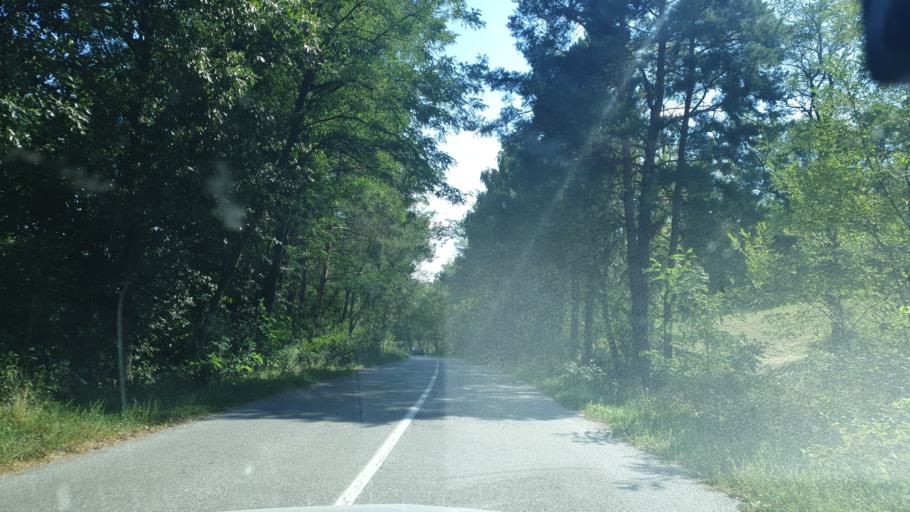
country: RS
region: Central Serbia
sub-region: Zlatiborski Okrug
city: Kosjeric
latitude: 44.0625
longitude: 20.0215
